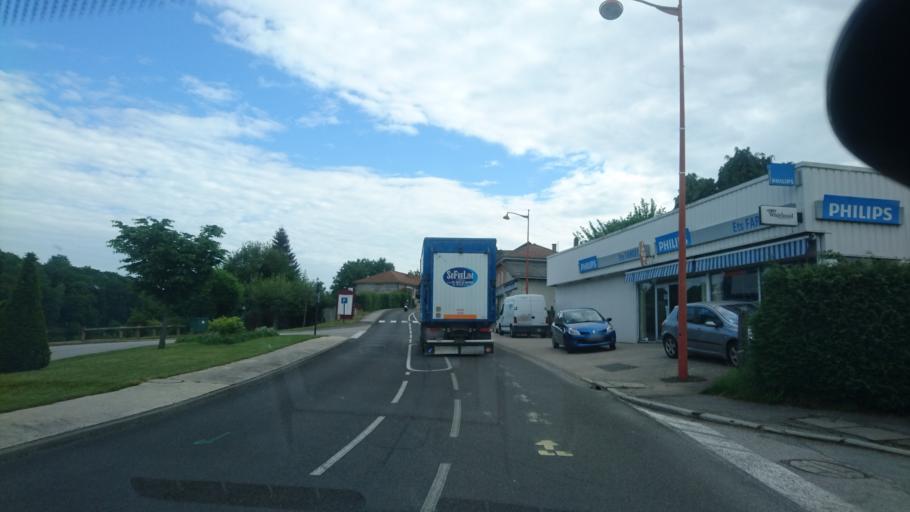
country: FR
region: Limousin
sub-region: Departement de la Haute-Vienne
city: Chateauneuf-la-Foret
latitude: 45.7098
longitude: 1.5989
